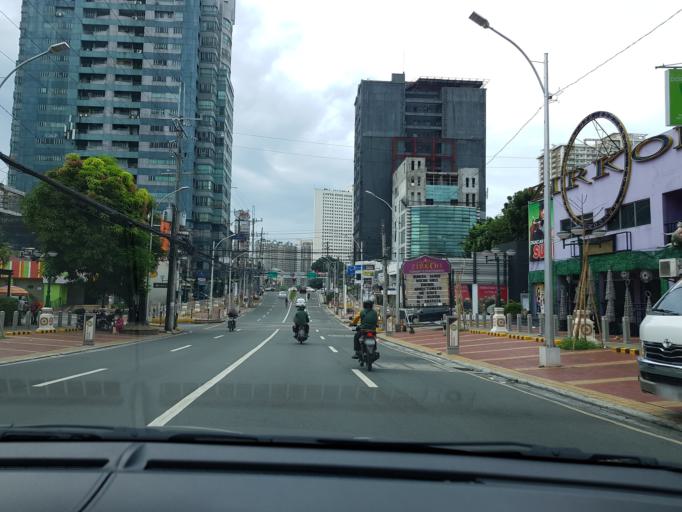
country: PH
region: Calabarzon
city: Del Monte
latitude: 14.6301
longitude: 121.0343
